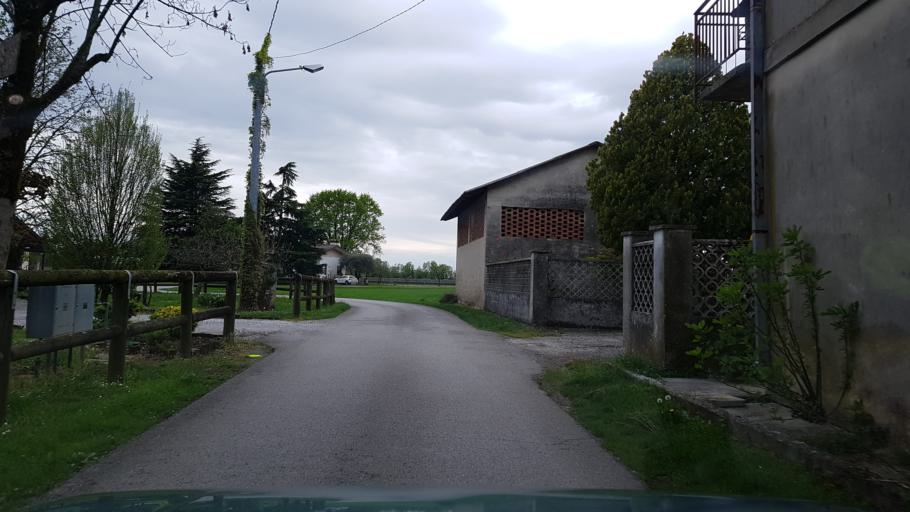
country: IT
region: Friuli Venezia Giulia
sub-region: Provincia di Gorizia
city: Moraro
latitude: 45.9332
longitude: 13.4781
